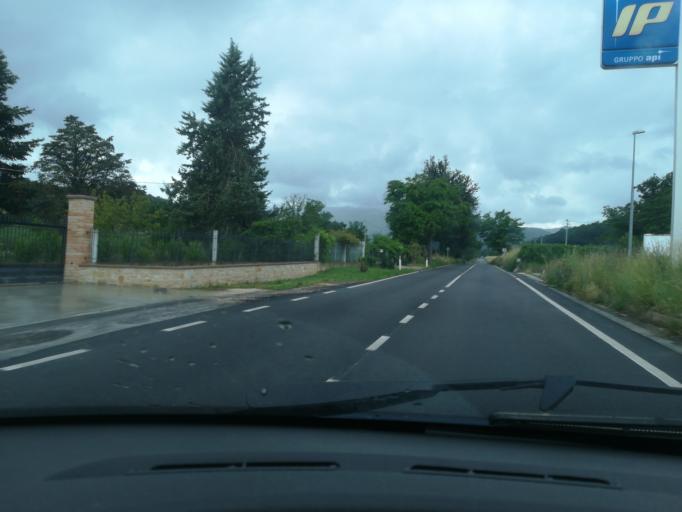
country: IT
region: The Marches
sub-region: Provincia di Macerata
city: San Ginesio
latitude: 43.0885
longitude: 13.3089
